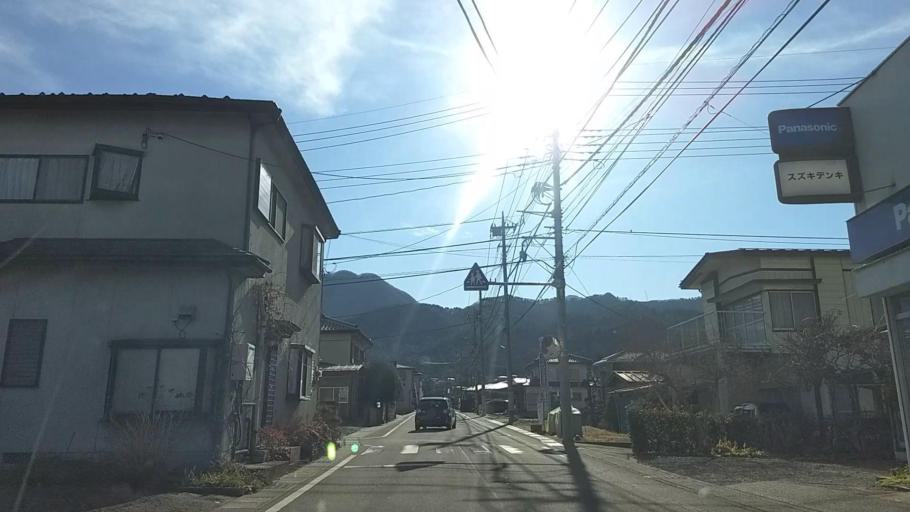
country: JP
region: Yamanashi
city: Otsuki
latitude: 35.5425
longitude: 138.9085
